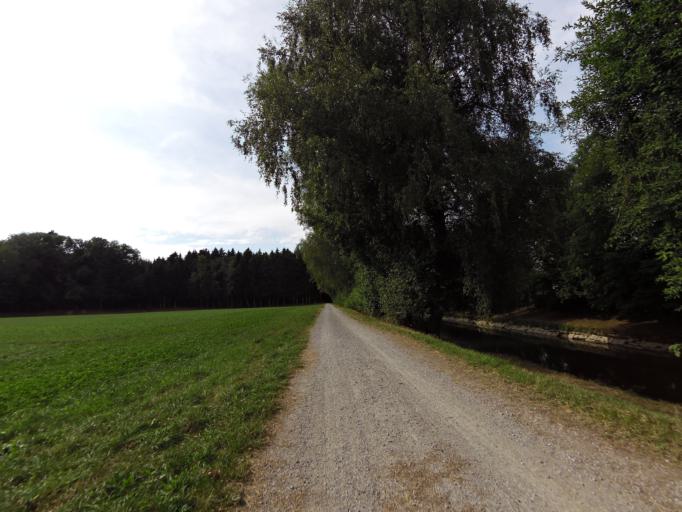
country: CH
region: Zurich
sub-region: Bezirk Buelach
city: Glattbrugg
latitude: 47.4401
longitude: 8.5543
